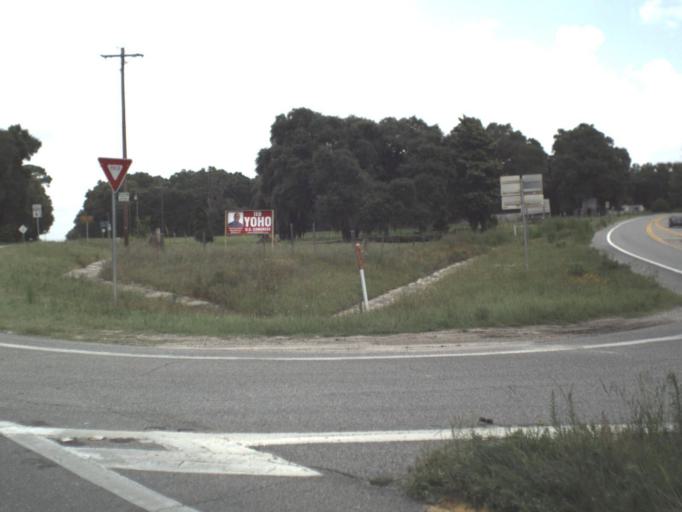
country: US
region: Florida
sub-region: Madison County
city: Madison
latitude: 30.4693
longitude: -83.3754
